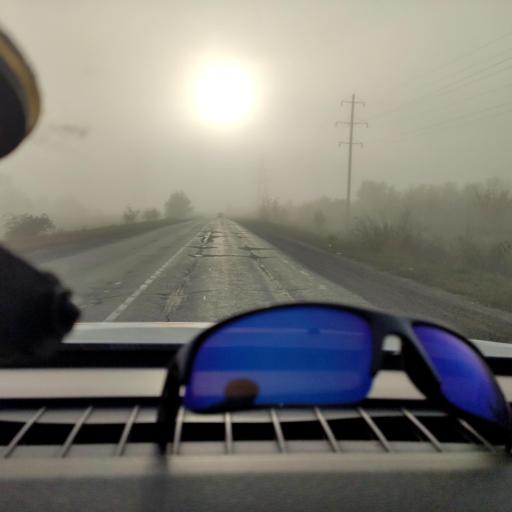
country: RU
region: Samara
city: Chapayevsk
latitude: 53.0023
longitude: 49.7545
